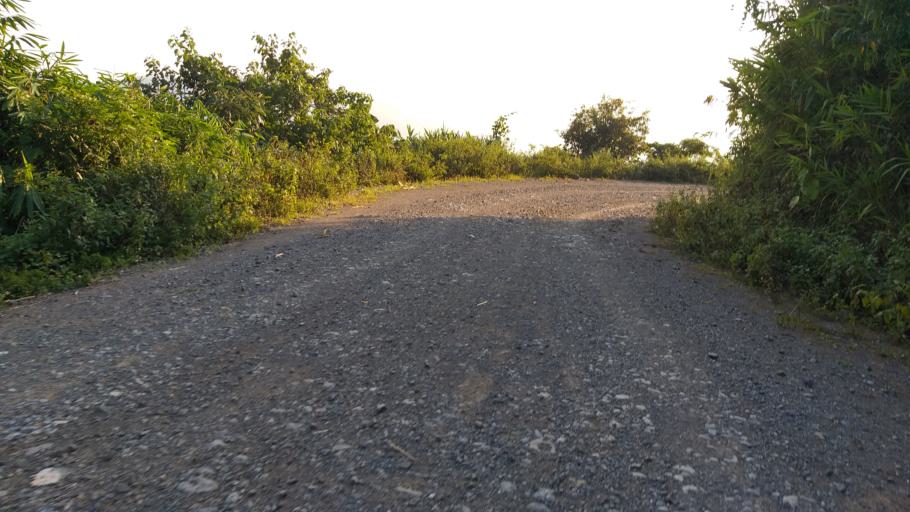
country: LA
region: Phongsali
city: Khoa
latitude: 21.2051
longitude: 102.5867
